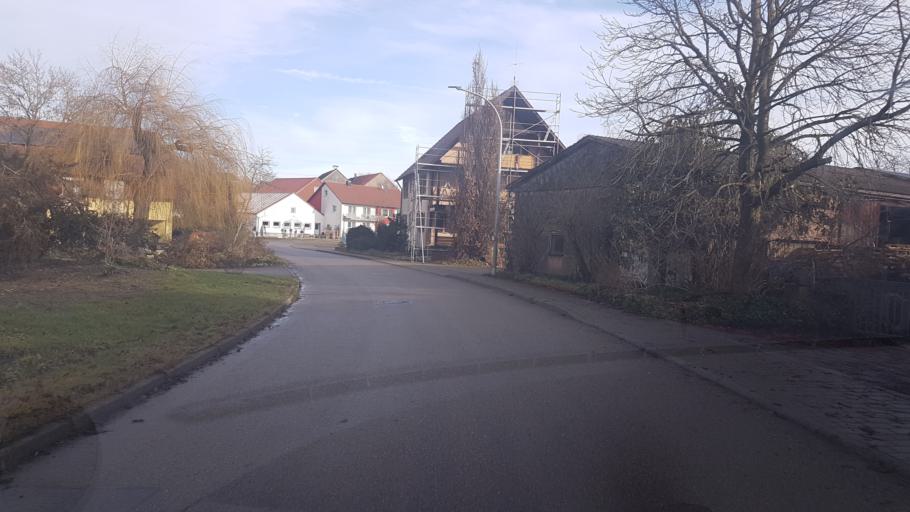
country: DE
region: Baden-Wuerttemberg
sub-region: Regierungsbezirk Stuttgart
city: Kupferzell
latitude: 49.2107
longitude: 9.7276
